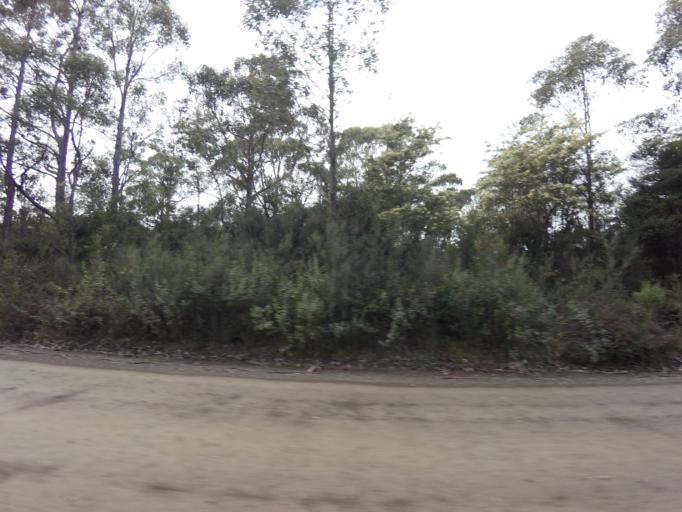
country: AU
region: Tasmania
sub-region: Huon Valley
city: Geeveston
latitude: -43.4604
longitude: 146.9000
